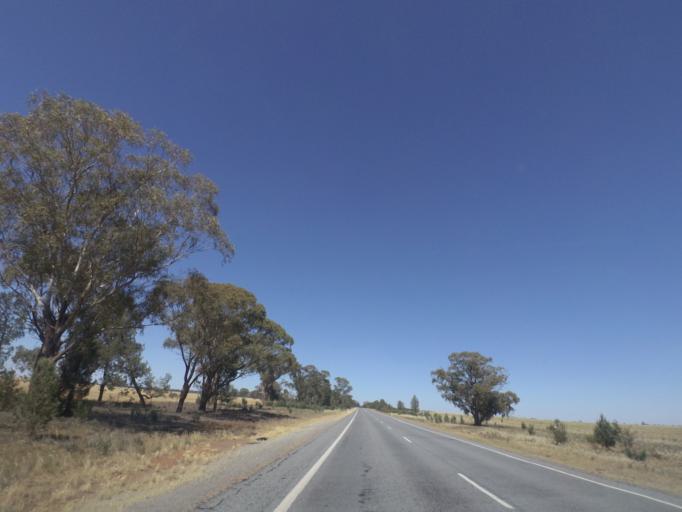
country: AU
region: New South Wales
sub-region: Narrandera
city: Narrandera
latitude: -34.4130
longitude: 146.8696
